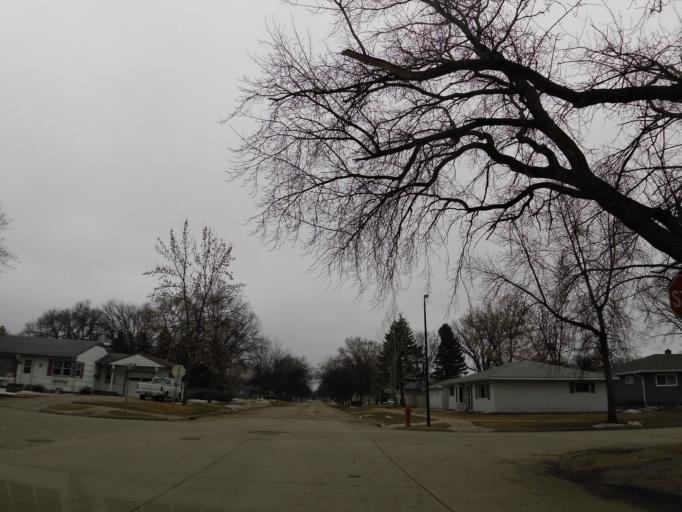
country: US
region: North Dakota
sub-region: Walsh County
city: Grafton
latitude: 48.4105
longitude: -97.4110
